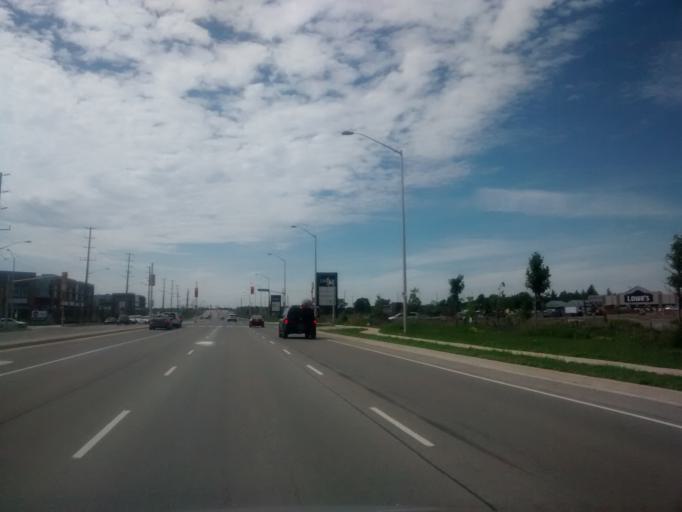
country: CA
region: Ontario
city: Burlington
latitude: 43.4098
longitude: -79.8122
